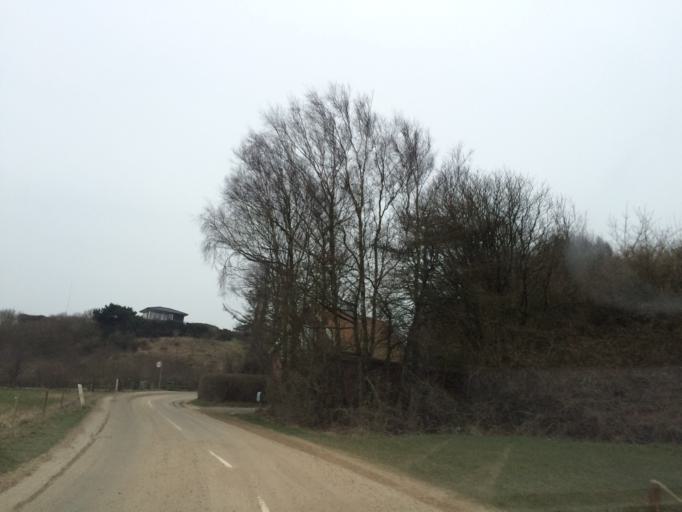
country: DK
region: Central Jutland
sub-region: Lemvig Kommune
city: Lemvig
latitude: 56.5837
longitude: 8.2810
